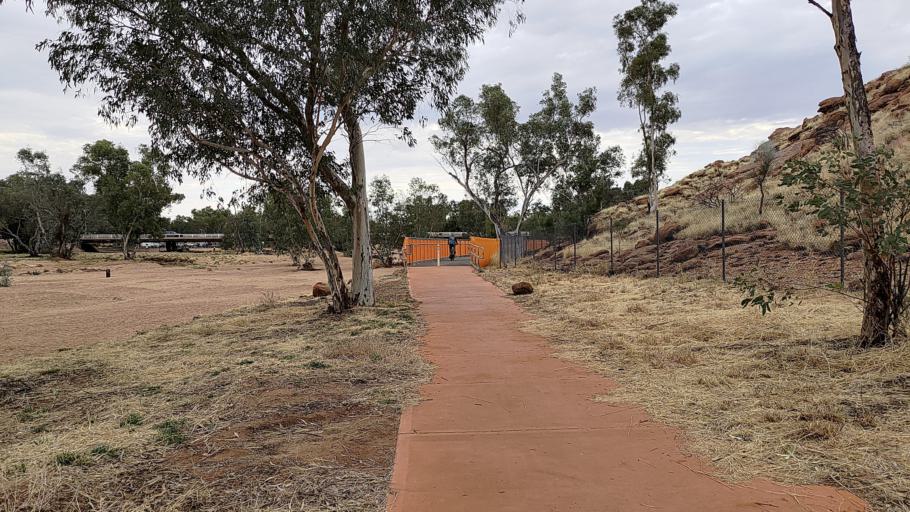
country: AU
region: Northern Territory
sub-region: Alice Springs
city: Alice Springs
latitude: -23.7046
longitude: 133.8834
